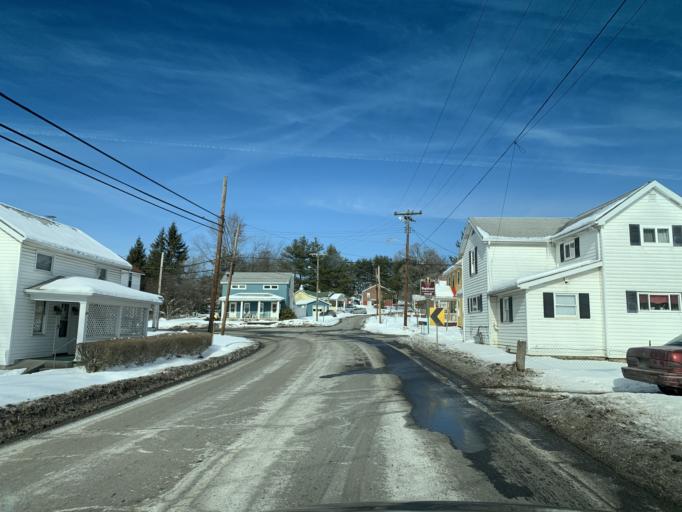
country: US
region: Maryland
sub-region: Allegany County
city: Frostburg
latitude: 39.6458
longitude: -78.9223
